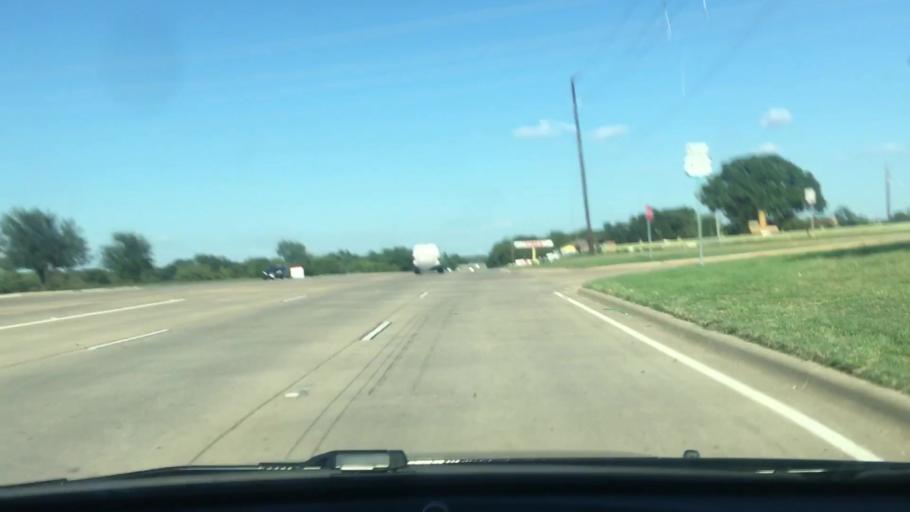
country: US
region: Texas
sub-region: Denton County
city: Denton
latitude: 33.2352
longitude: -97.0732
